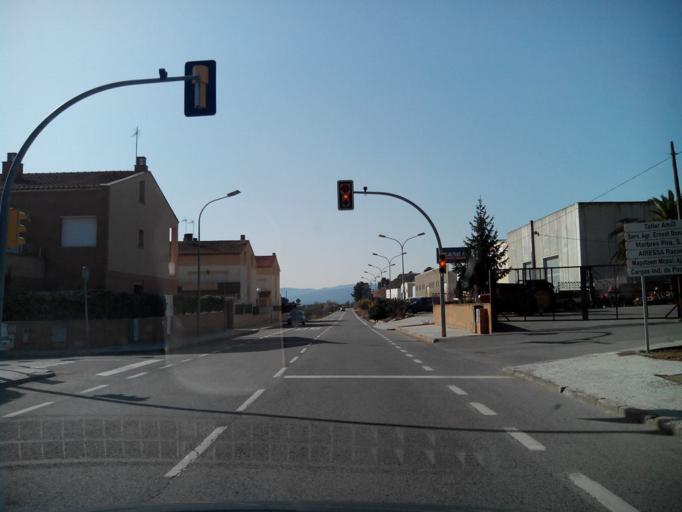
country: ES
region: Catalonia
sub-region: Provincia de Tarragona
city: Blancafort
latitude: 41.4206
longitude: 1.2004
